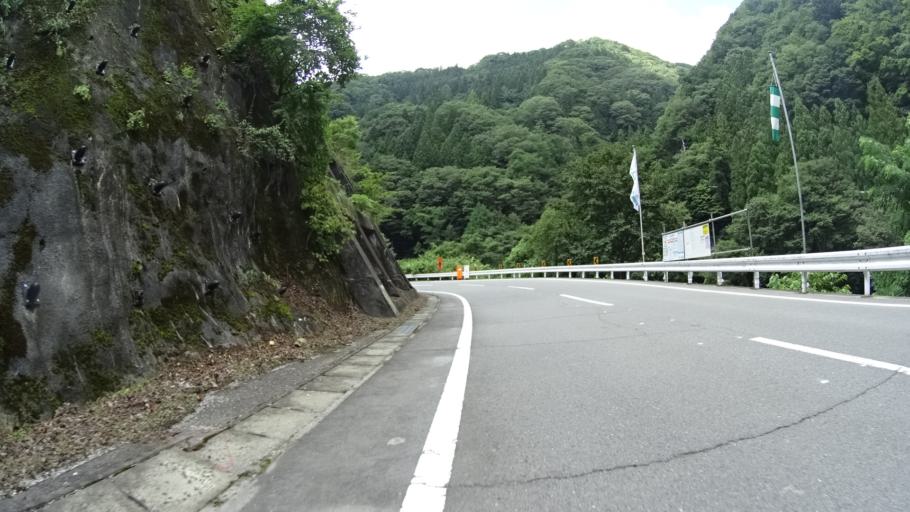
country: JP
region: Gunma
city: Tomioka
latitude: 36.0767
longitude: 138.7079
